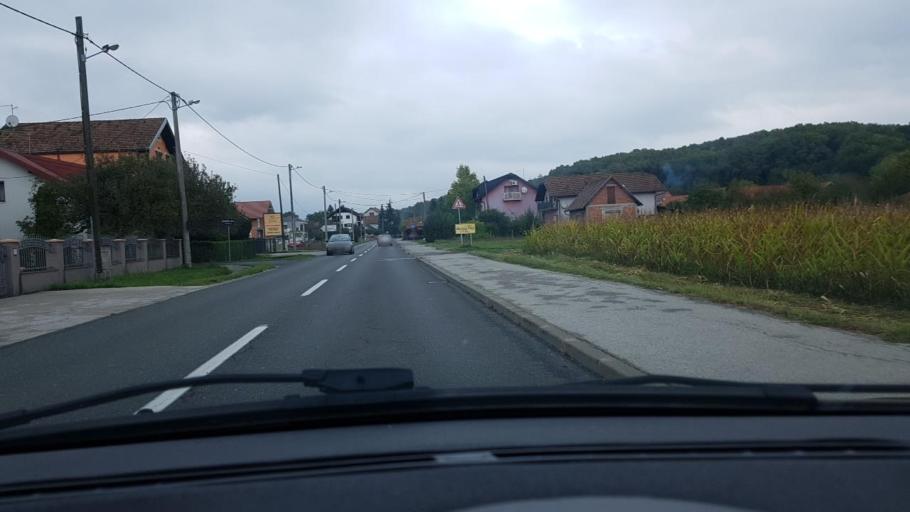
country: HR
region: Grad Zagreb
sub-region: Sesvete
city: Sesvete
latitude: 45.8592
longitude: 16.1139
